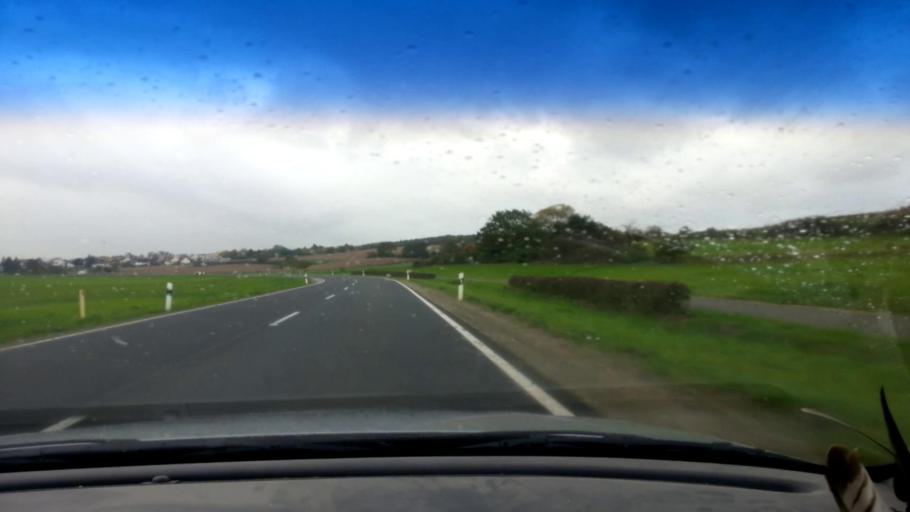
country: DE
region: Bavaria
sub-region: Upper Franconia
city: Stegaurach
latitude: 49.8688
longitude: 10.8280
